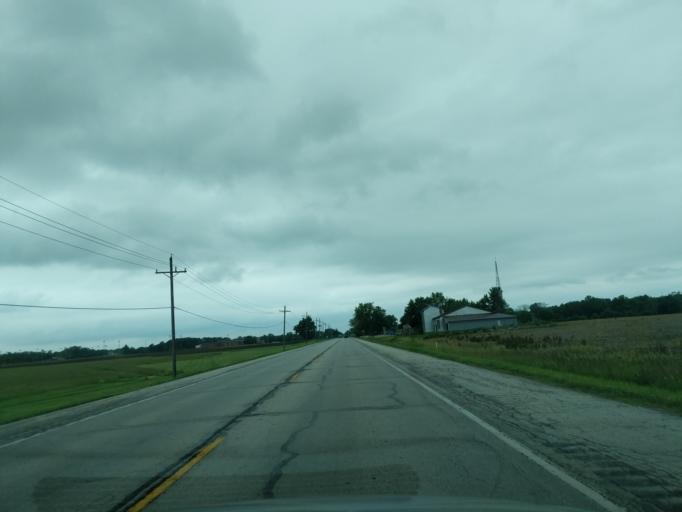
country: US
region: Indiana
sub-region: Hamilton County
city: Arcadia
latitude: 40.1567
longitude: -86.0133
